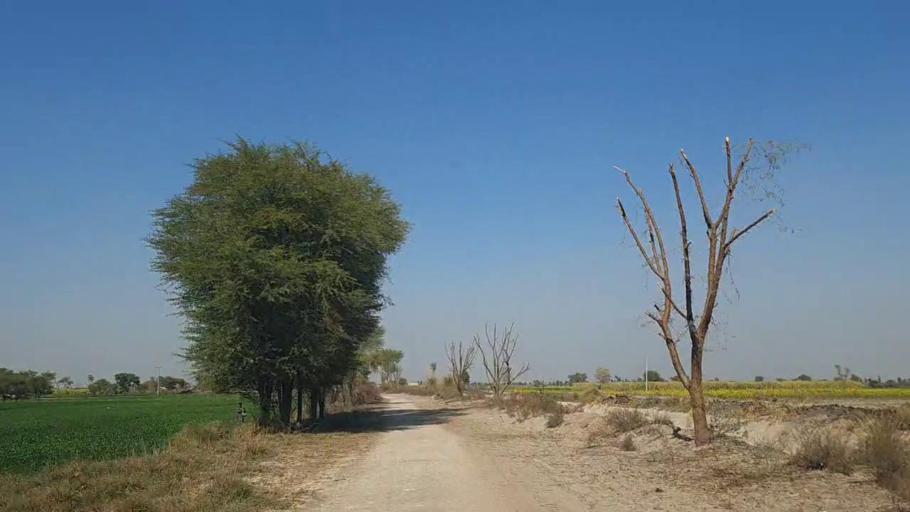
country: PK
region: Sindh
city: Sakrand
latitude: 26.2701
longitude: 68.2210
